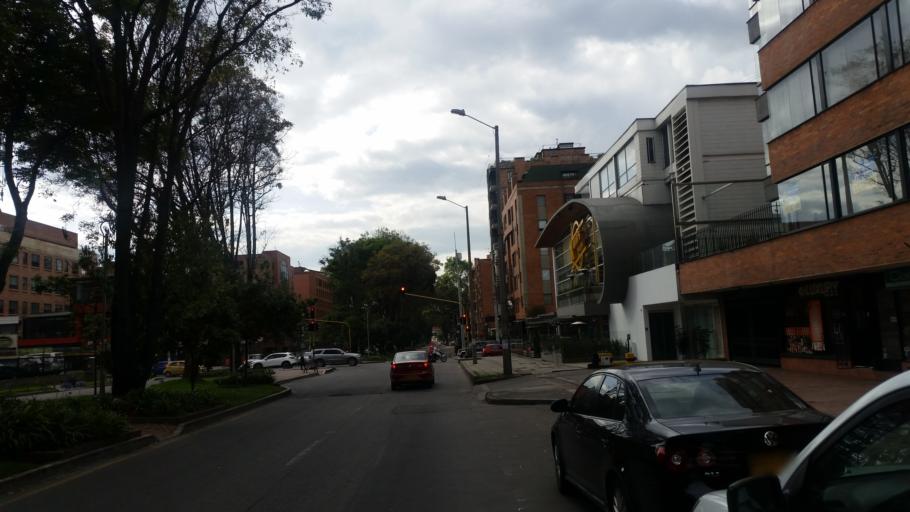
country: CO
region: Bogota D.C.
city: Barrio San Luis
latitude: 4.6782
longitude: -74.0478
